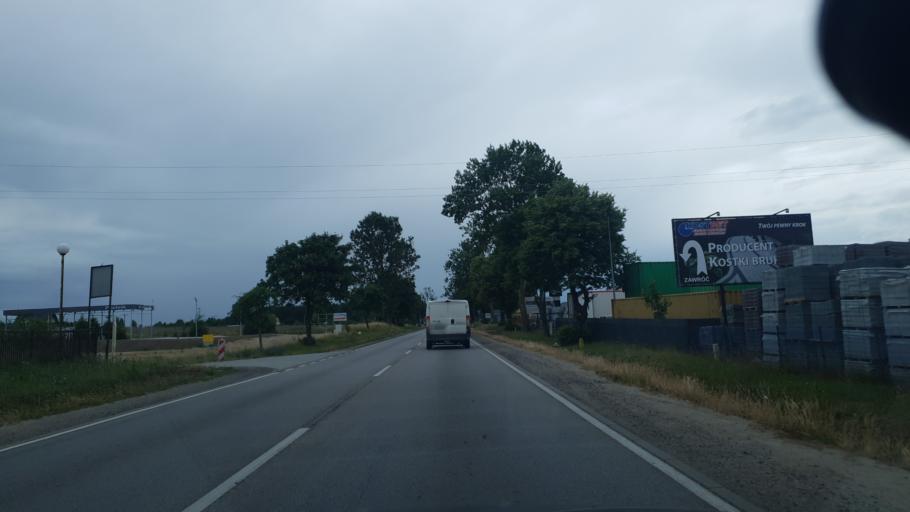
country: PL
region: Pomeranian Voivodeship
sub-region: Powiat kartuski
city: Banino
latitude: 54.4053
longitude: 18.3649
